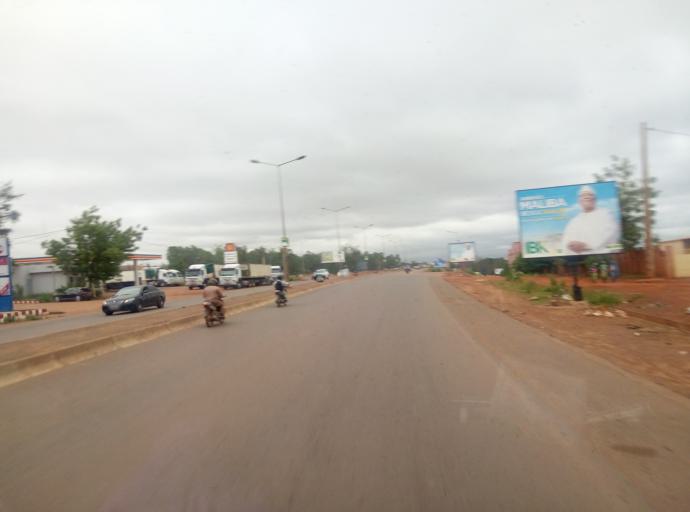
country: ML
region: Bamako
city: Bamako
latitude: 12.6109
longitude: -7.9949
